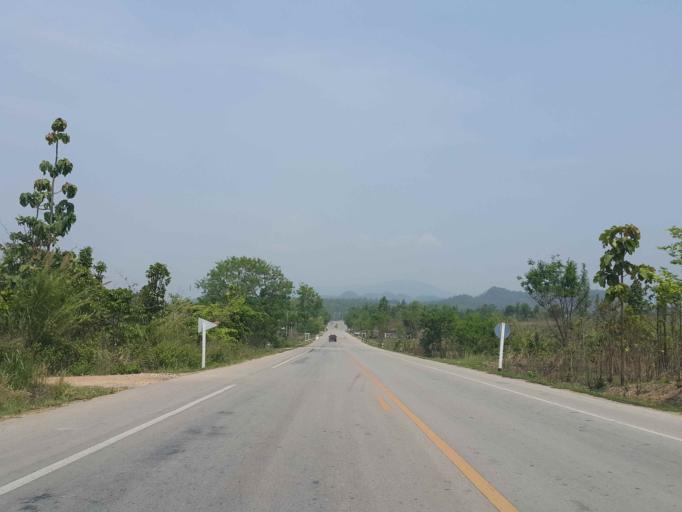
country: TH
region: Chiang Mai
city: Mae Taeng
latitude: 19.0834
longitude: 98.9122
